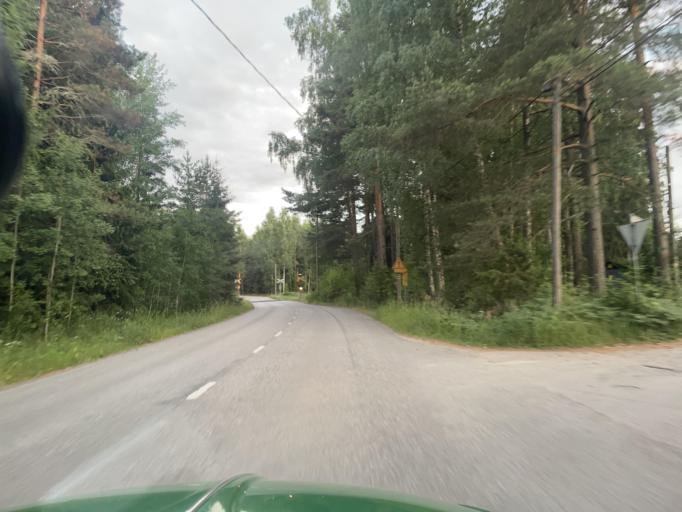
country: FI
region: Uusimaa
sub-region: Helsinki
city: Lohja
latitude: 60.2355
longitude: 24.0691
